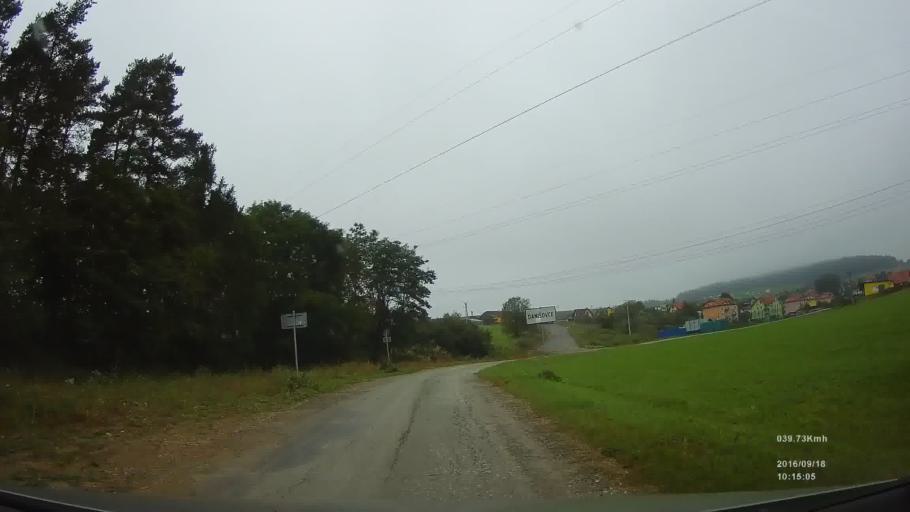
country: SK
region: Kosicky
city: Spisska Nova Ves
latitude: 48.9444
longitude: 20.6218
